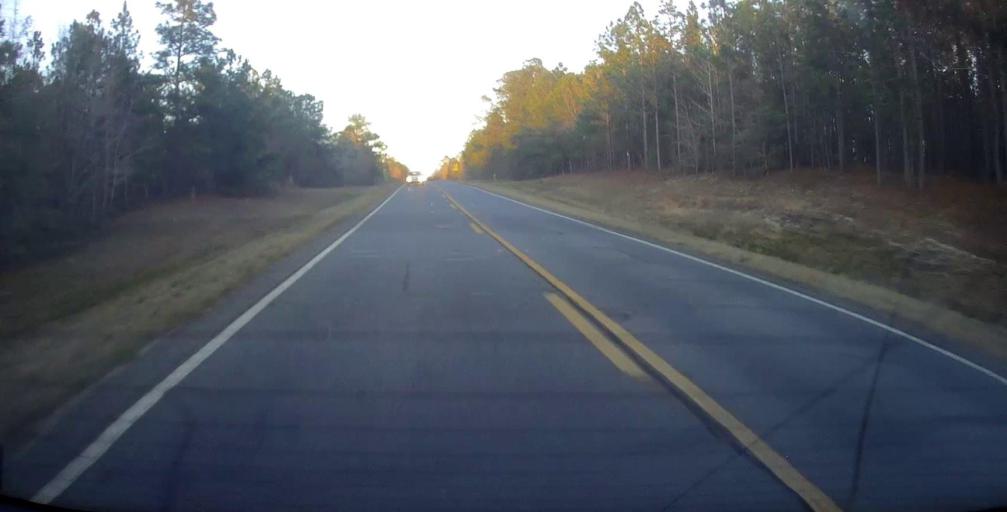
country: US
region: Georgia
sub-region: Dodge County
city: Eastman
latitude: 32.2710
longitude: -83.1209
